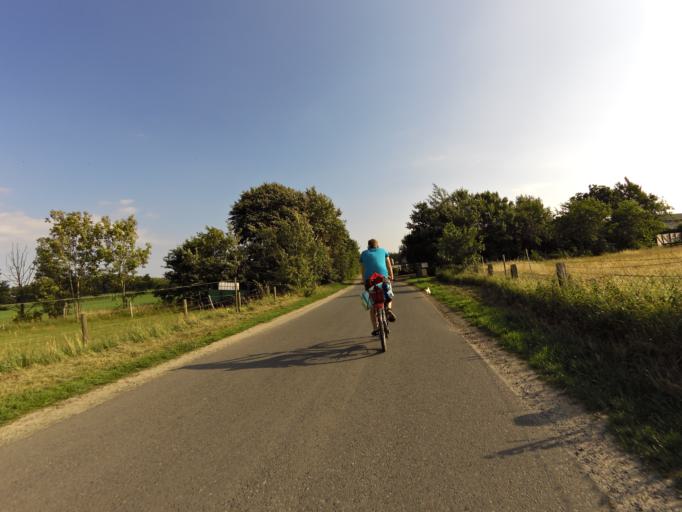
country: DE
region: Lower Saxony
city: Nordholz
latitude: 53.8175
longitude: 8.5893
